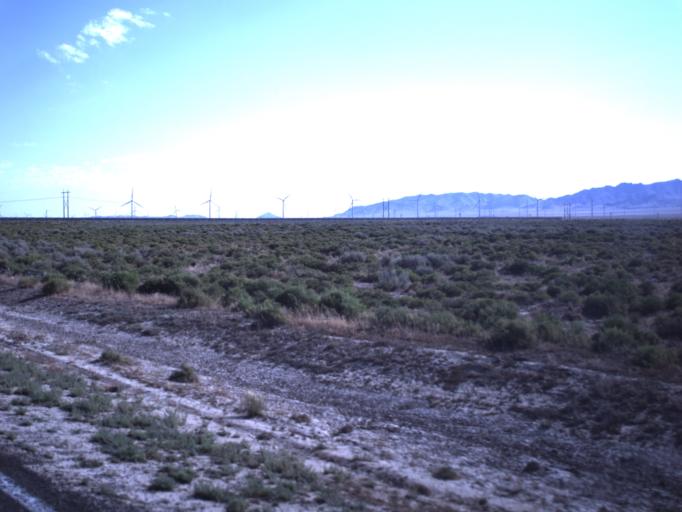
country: US
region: Utah
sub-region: Beaver County
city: Milford
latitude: 38.4812
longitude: -112.9911
